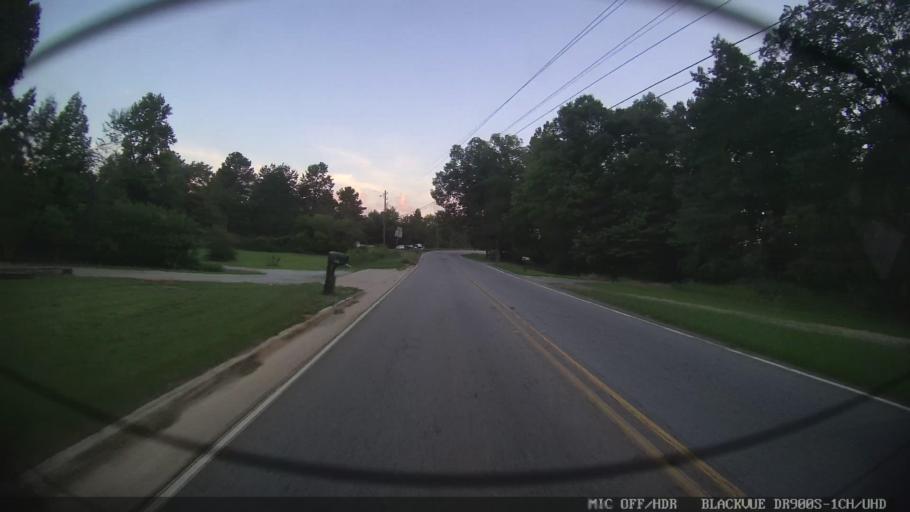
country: US
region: Georgia
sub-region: Forsyth County
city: Cumming
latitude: 34.2958
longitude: -84.1636
